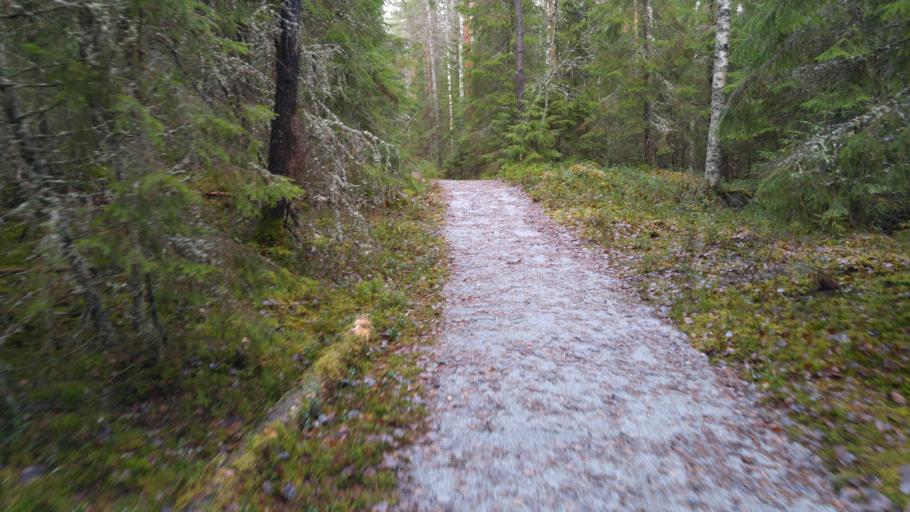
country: FI
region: Pirkanmaa
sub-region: Tampere
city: Kangasala
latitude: 61.6023
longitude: 23.9921
